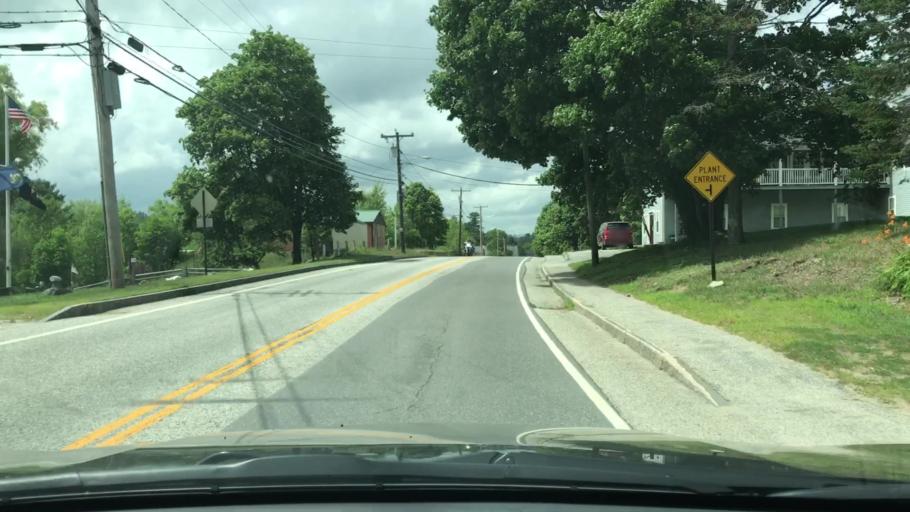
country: US
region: Maine
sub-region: Oxford County
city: Bethel
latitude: 44.3997
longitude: -70.7016
